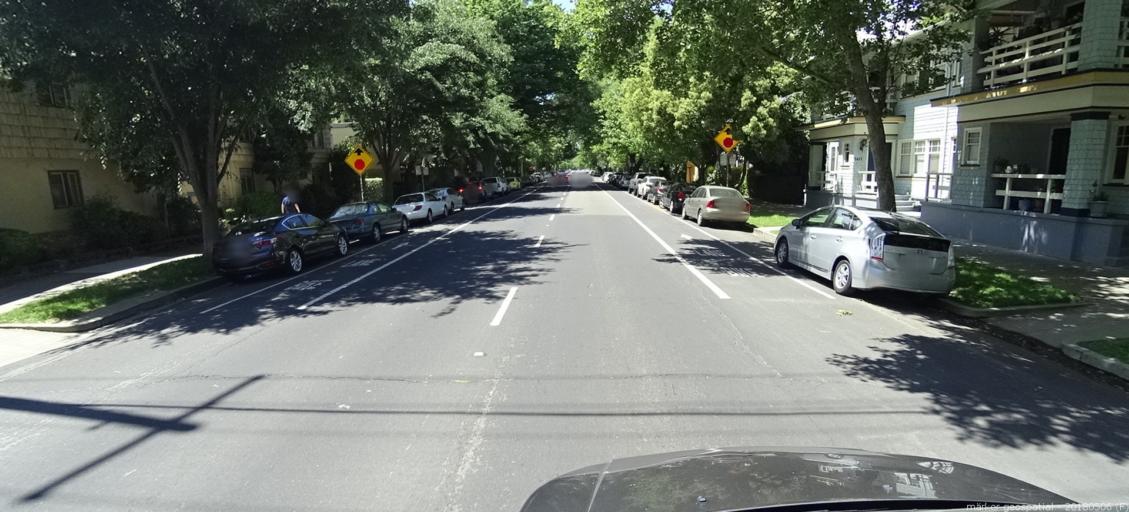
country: US
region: California
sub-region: Sacramento County
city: Sacramento
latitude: 38.5683
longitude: -121.4761
